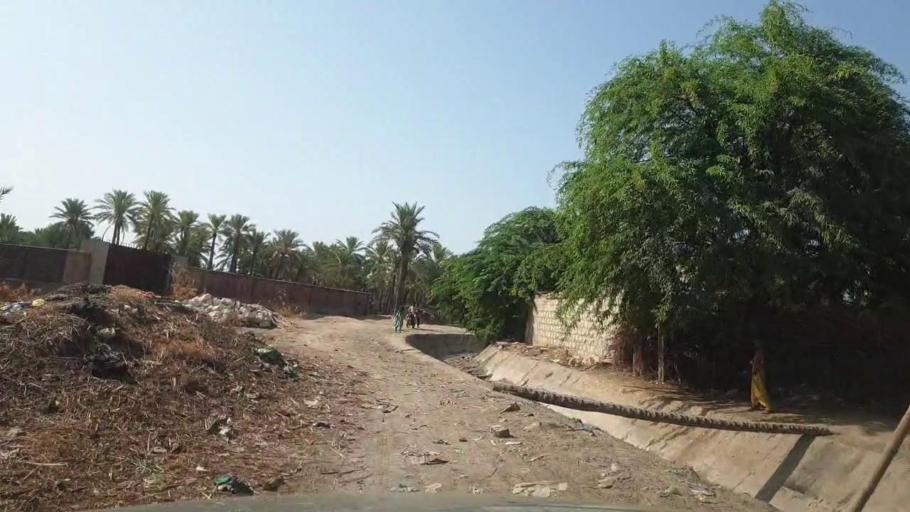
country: PK
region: Sindh
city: Rohri
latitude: 27.6598
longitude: 68.8838
